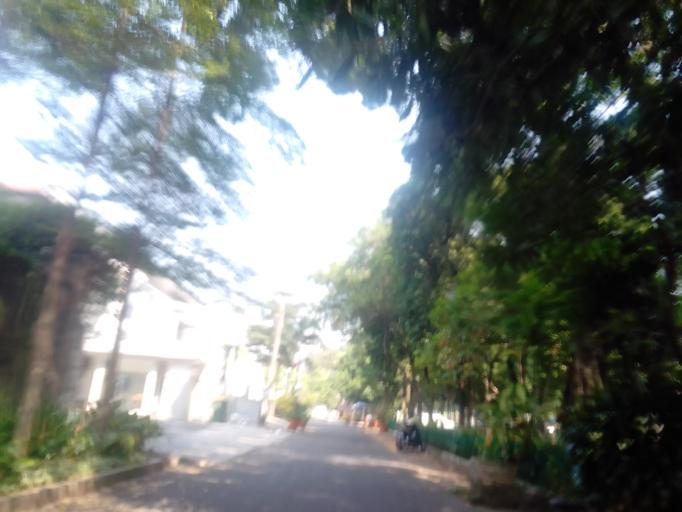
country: ID
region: Jakarta Raya
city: Jakarta
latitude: -6.2521
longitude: 106.7994
